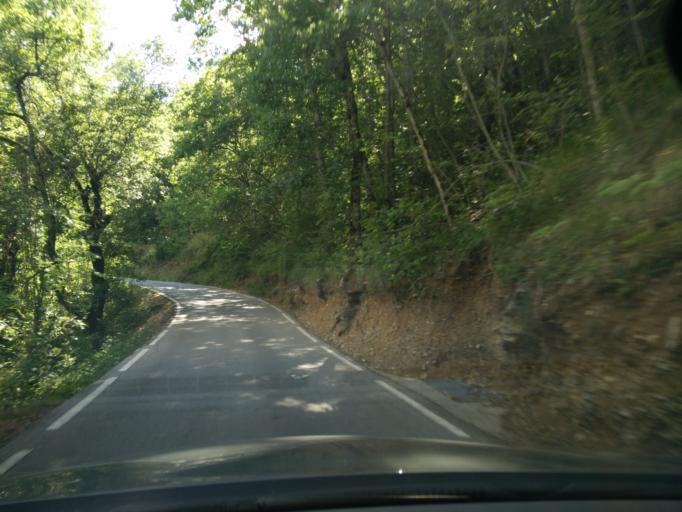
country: ES
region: Castille and Leon
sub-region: Provincia de Leon
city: Posada de Valdeon
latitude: 43.1807
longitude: -4.9037
